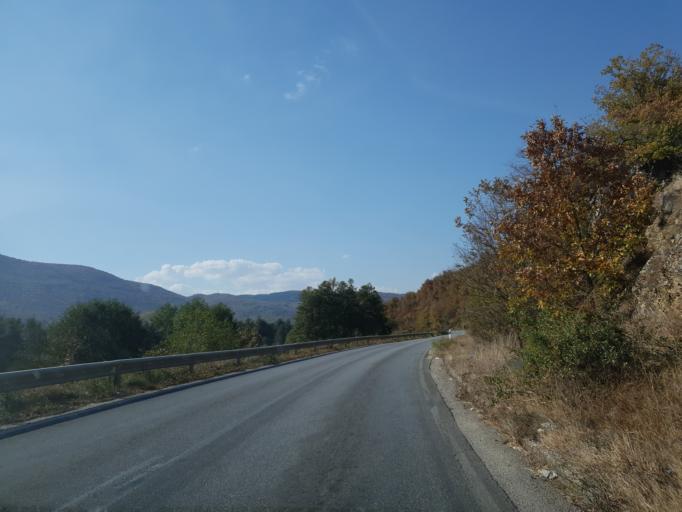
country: MK
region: Vranestica
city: Vranestica
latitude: 41.4682
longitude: 21.0193
